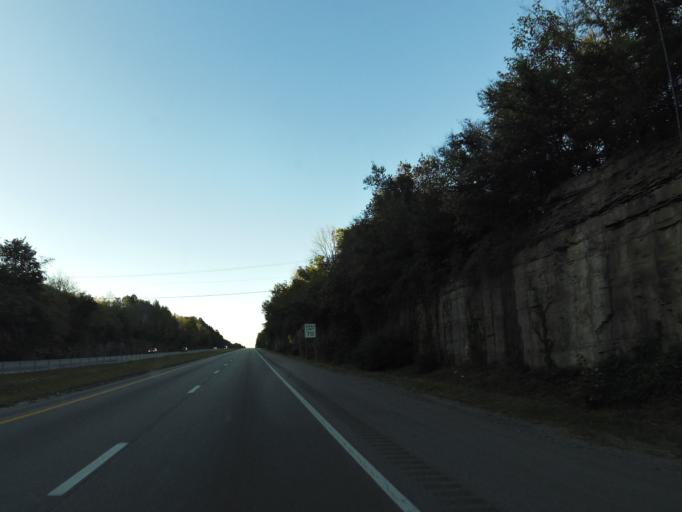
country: US
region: Kentucky
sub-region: Whitley County
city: Williamsburg
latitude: 36.7336
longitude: -84.1721
